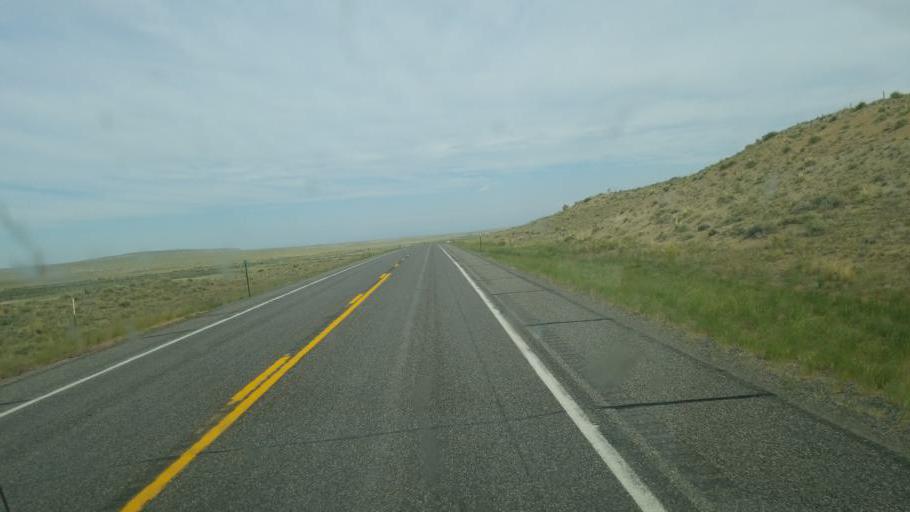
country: US
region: Wyoming
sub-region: Fremont County
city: Riverton
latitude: 43.2210
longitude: -108.0011
